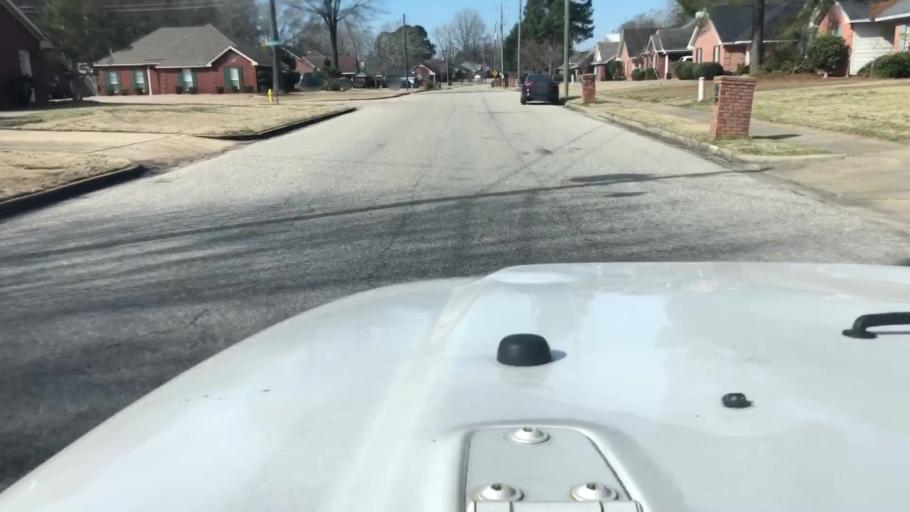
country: US
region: Alabama
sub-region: Elmore County
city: Blue Ridge
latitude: 32.4072
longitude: -86.1916
